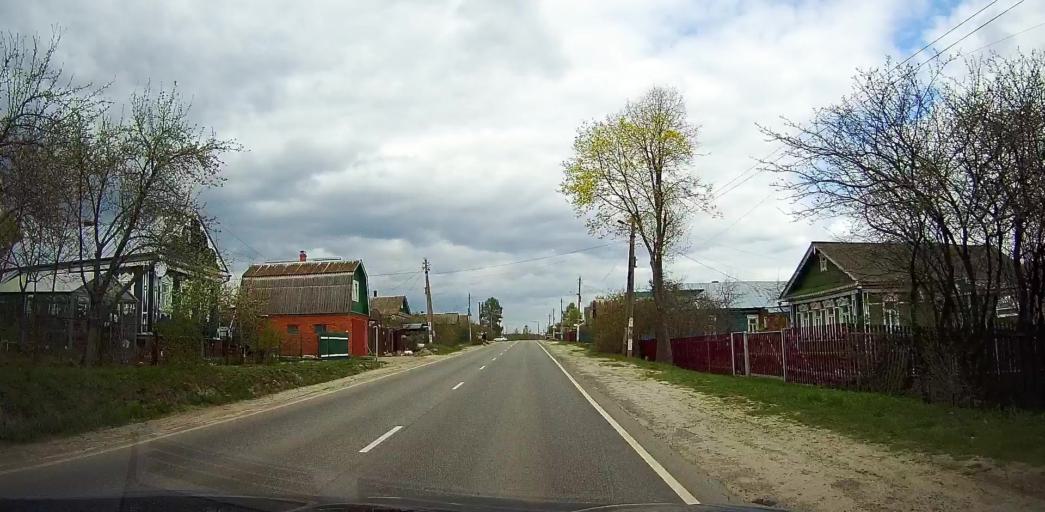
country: RU
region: Moskovskaya
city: Ashitkovo
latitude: 55.4566
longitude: 38.5963
